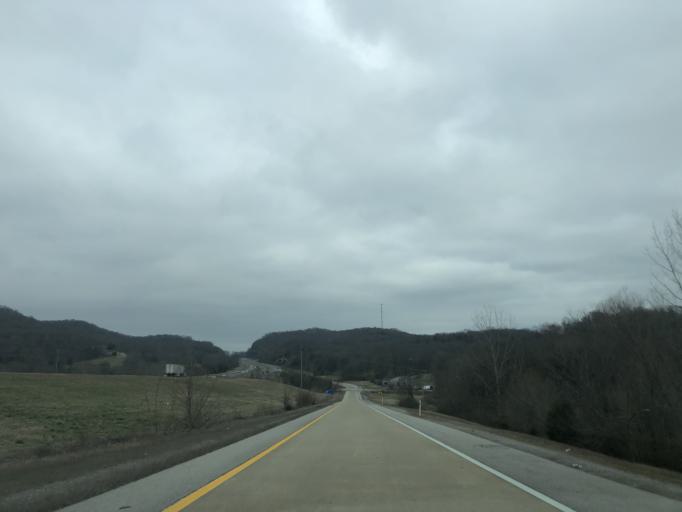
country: US
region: Tennessee
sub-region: Williamson County
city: Thompson's Station
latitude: 35.8127
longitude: -86.7787
